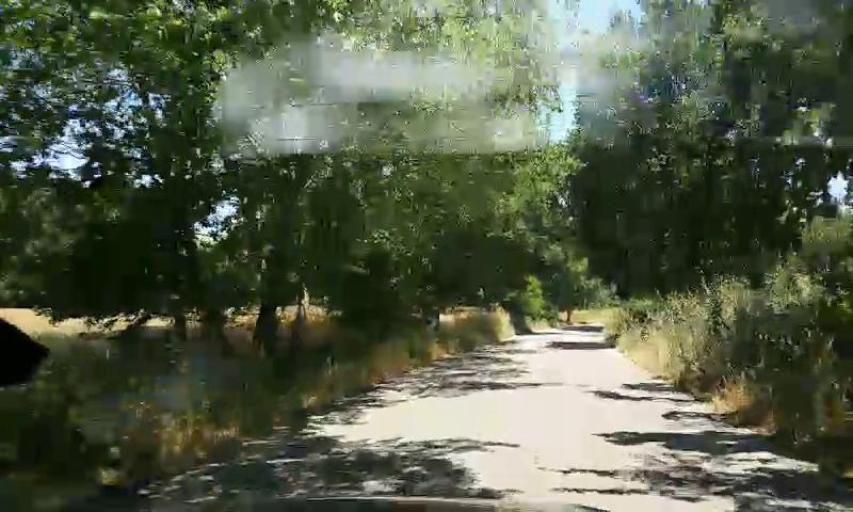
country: IT
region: Molise
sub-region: Provincia di Campobasso
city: San Giacomo degli Schiavoni
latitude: 41.9626
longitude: 14.9004
